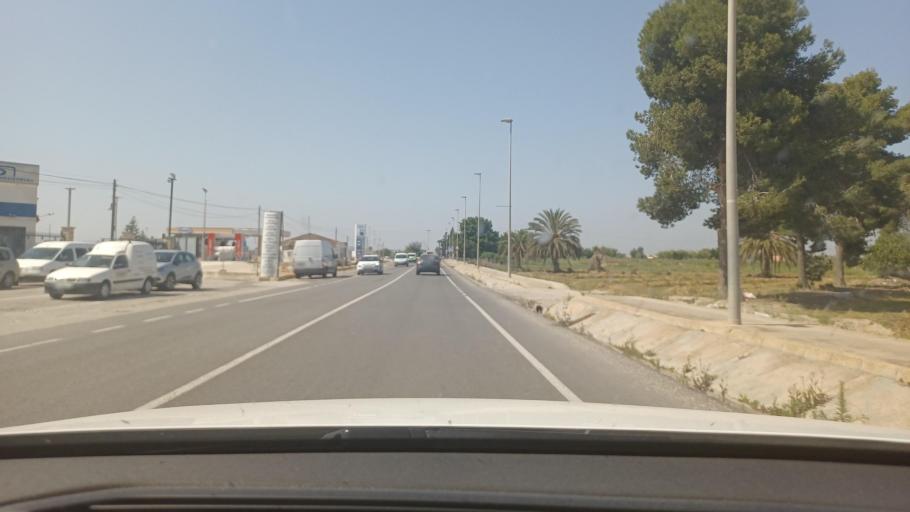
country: ES
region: Valencia
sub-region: Provincia de Alicante
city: Dolores
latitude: 38.1320
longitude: -0.7753
